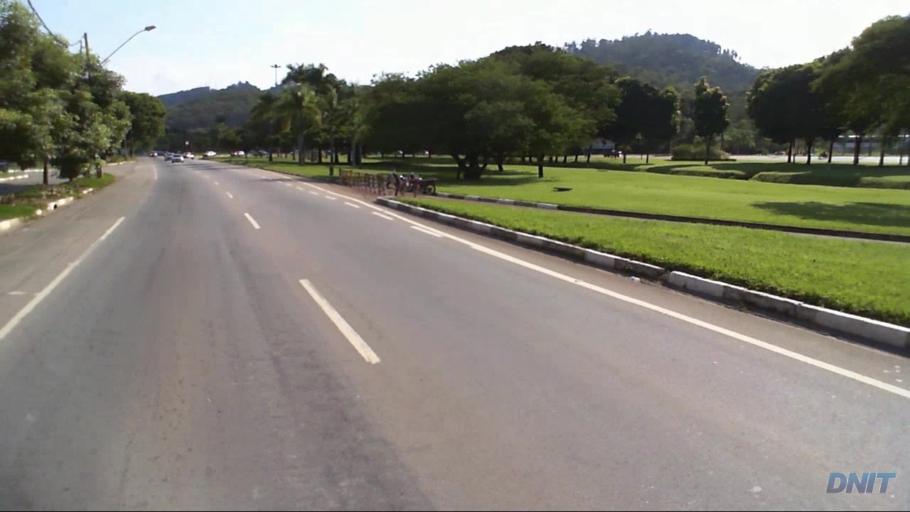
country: BR
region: Minas Gerais
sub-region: Ipatinga
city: Ipatinga
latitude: -19.4850
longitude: -42.5535
